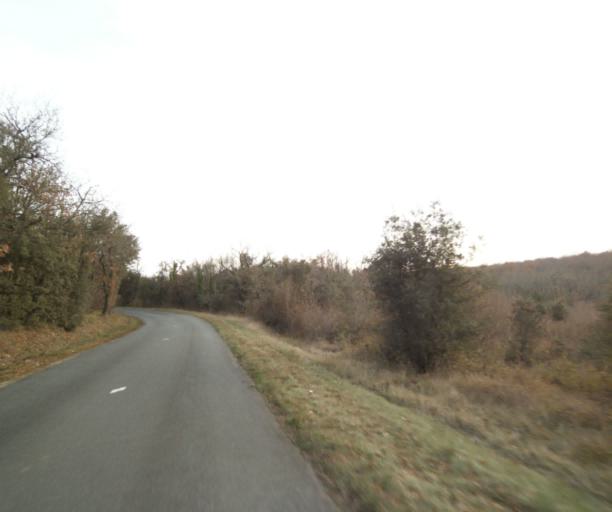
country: FR
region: Poitou-Charentes
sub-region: Departement de la Charente-Maritime
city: Fontcouverte
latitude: 45.8115
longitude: -0.5934
